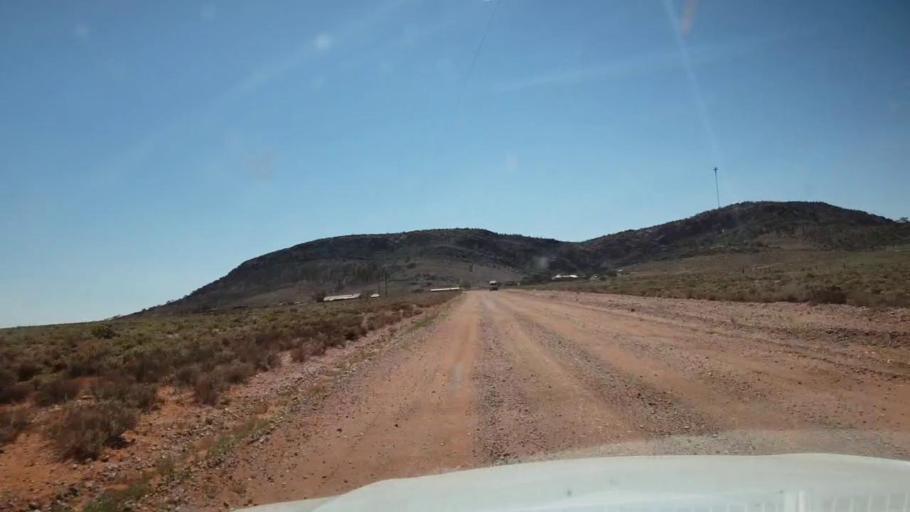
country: AU
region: South Australia
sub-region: Whyalla
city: Whyalla
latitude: -32.6898
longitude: 137.1279
